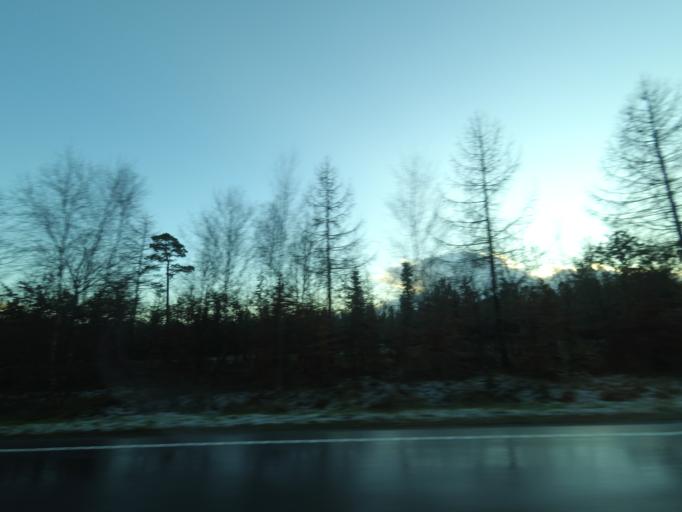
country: DK
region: Central Jutland
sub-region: Ikast-Brande Kommune
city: Brande
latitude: 56.0106
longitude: 9.0559
